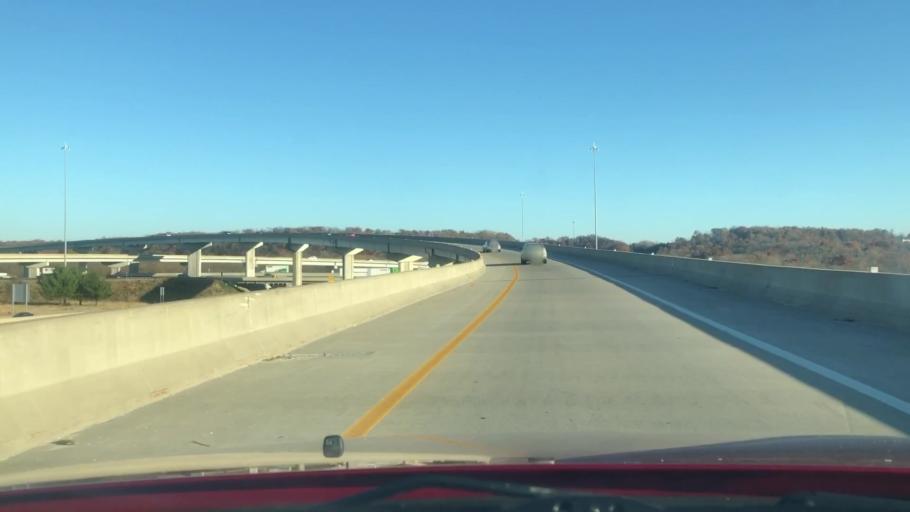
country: US
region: Missouri
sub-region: Christian County
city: Nixa
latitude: 37.1285
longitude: -93.2339
